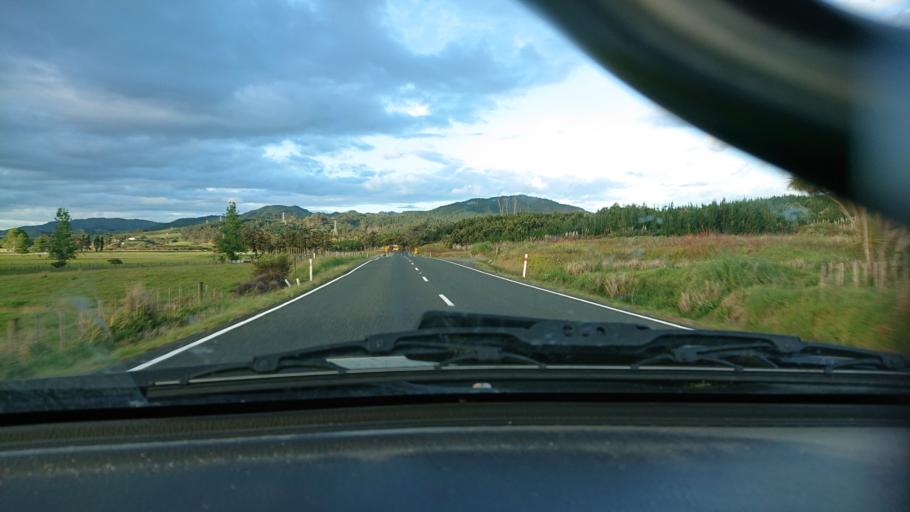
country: NZ
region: Auckland
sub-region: Auckland
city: Parakai
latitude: -36.5166
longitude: 174.4507
